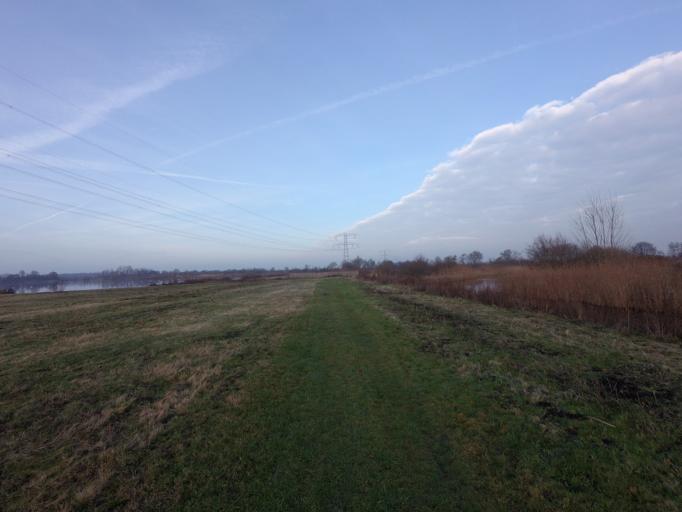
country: NL
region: Utrecht
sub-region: Gemeente Woerden
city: Woerden
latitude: 52.0846
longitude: 4.9278
